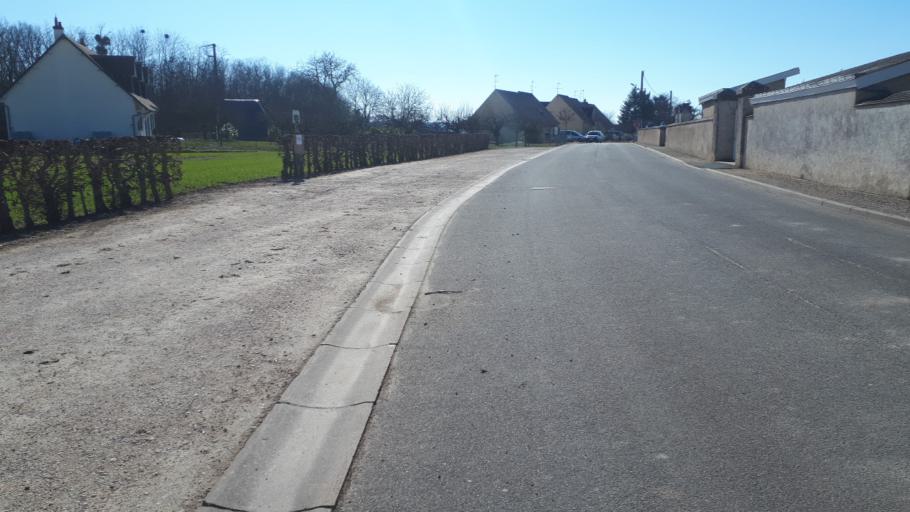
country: FR
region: Centre
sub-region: Departement du Loir-et-Cher
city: Villiers-sur-Loir
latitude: 47.7908
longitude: 0.9694
